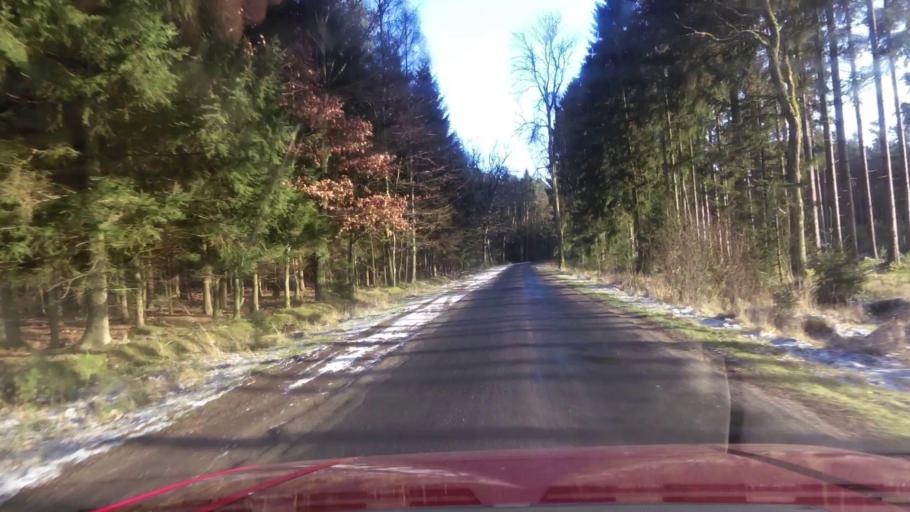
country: PL
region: West Pomeranian Voivodeship
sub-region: Powiat bialogardzki
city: Bialogard
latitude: 54.0990
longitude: 16.0478
